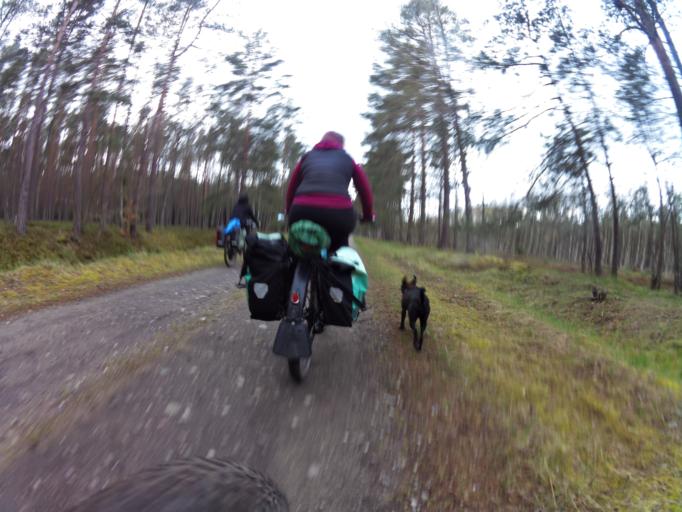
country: PL
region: Pomeranian Voivodeship
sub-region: Powiat slupski
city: Kepice
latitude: 54.3143
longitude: 16.8163
